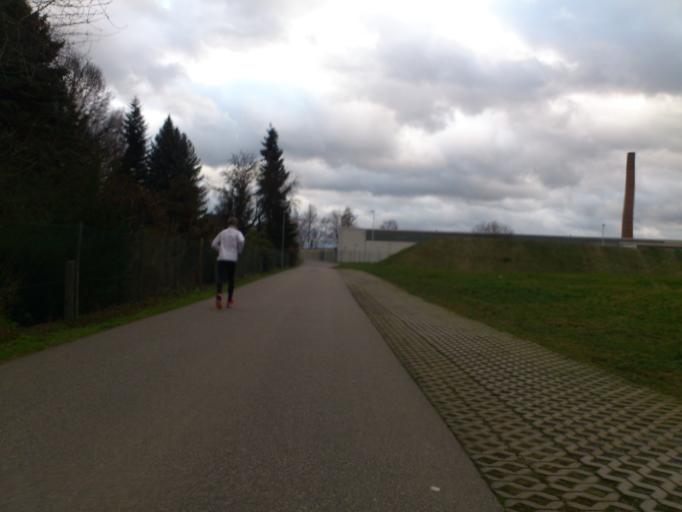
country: DE
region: Saxony
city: Chemnitz
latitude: 50.8035
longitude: 12.9521
